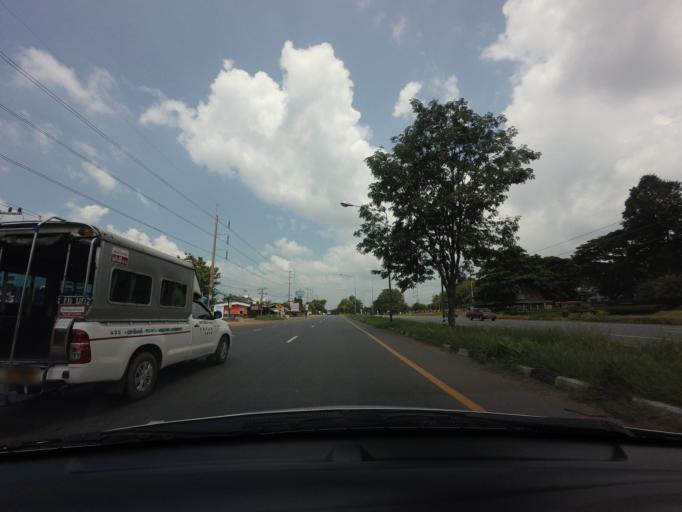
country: TH
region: Prachin Buri
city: Kabin Buri
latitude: 13.9586
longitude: 101.7262
